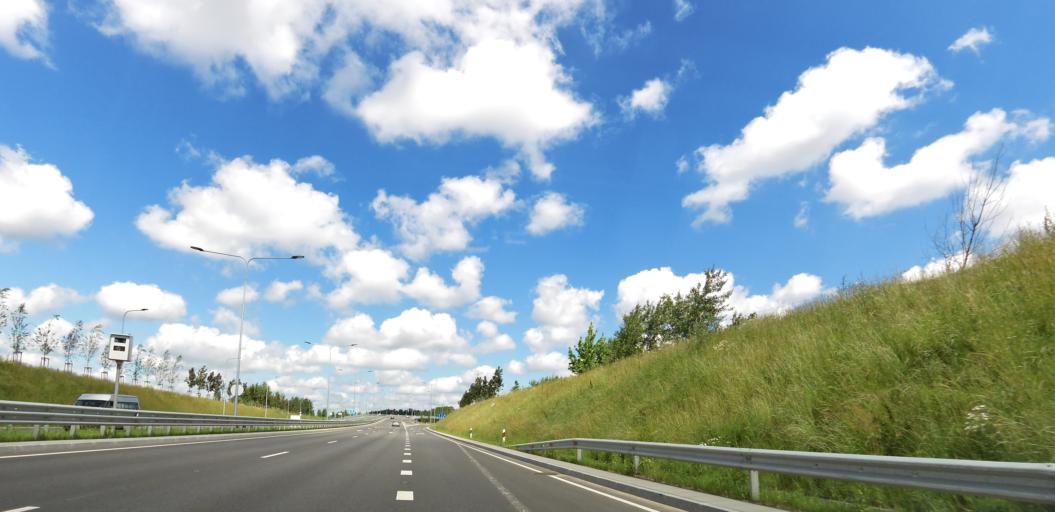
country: LT
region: Vilnius County
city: Pasilaiciai
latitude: 54.7319
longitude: 25.2083
